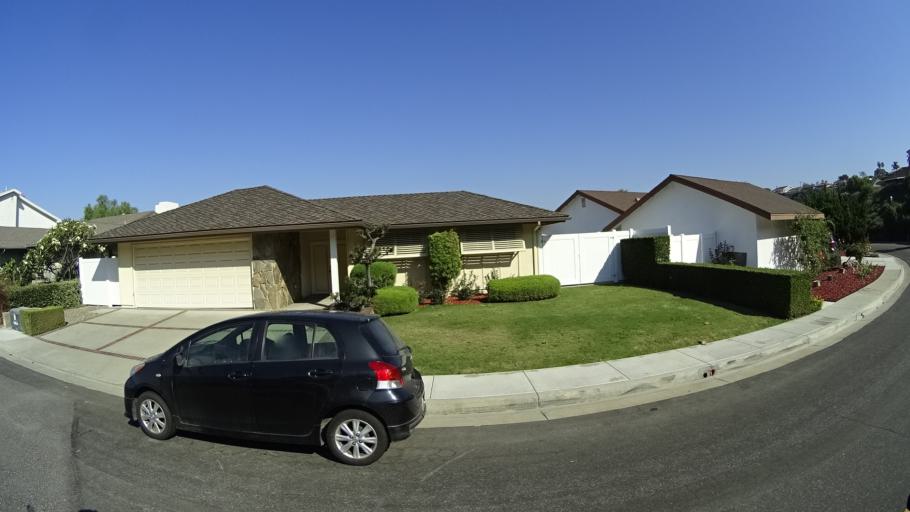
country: US
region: California
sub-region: Orange County
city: San Clemente
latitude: 33.4339
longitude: -117.6093
